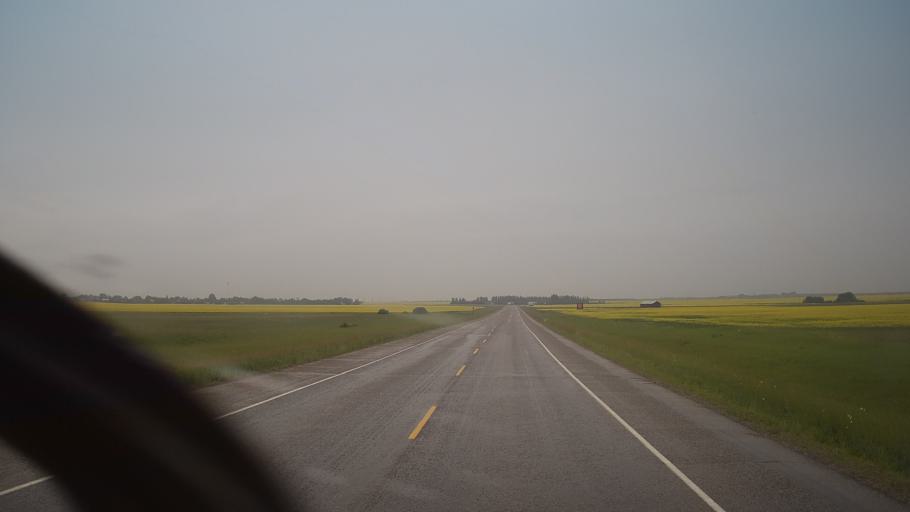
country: CA
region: Saskatchewan
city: Wilkie
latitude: 52.1937
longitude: -108.4271
